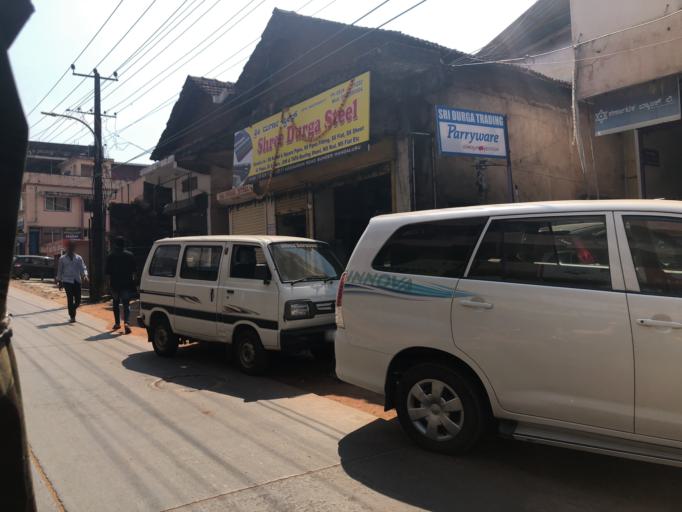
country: IN
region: Karnataka
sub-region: Dakshina Kannada
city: Mangalore
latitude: 12.8671
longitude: 74.8332
